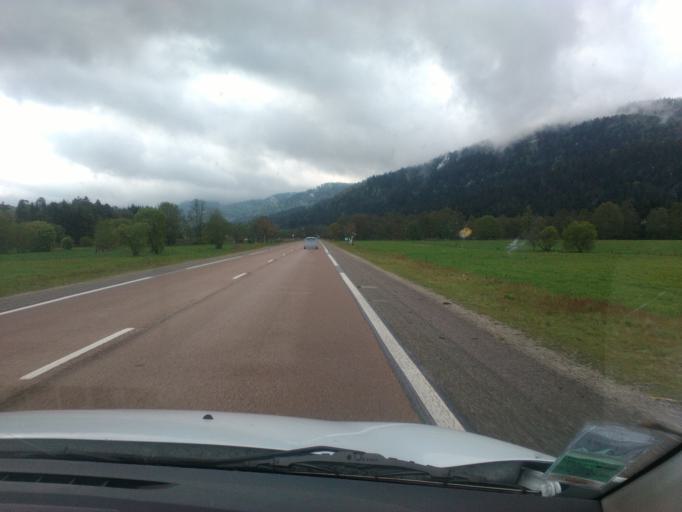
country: FR
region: Lorraine
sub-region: Departement des Vosges
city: Vagney
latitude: 48.0039
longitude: 6.7115
